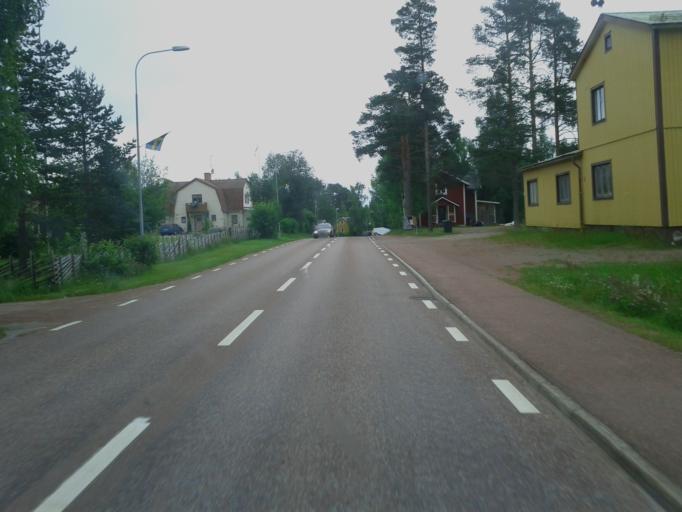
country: NO
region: Hedmark
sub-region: Trysil
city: Innbygda
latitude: 61.6949
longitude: 13.1286
